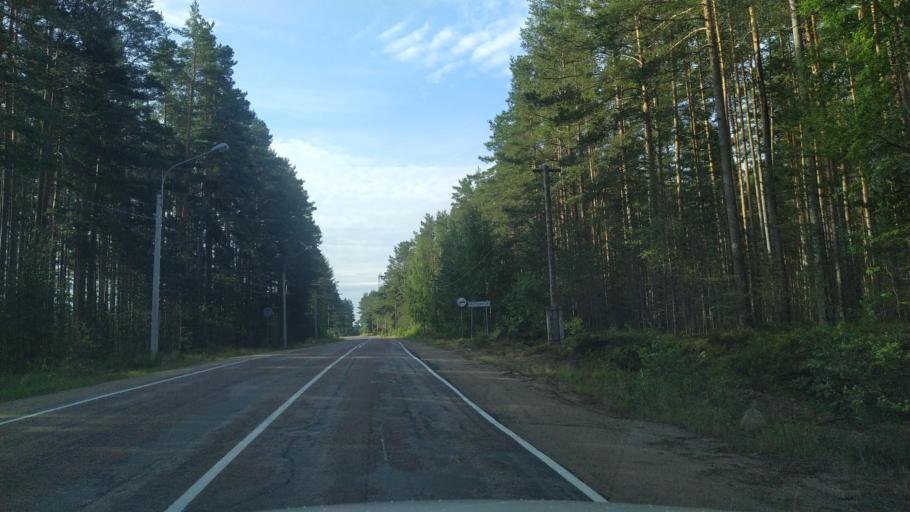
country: RU
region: Leningrad
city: Priozersk
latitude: 60.9672
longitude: 30.2866
